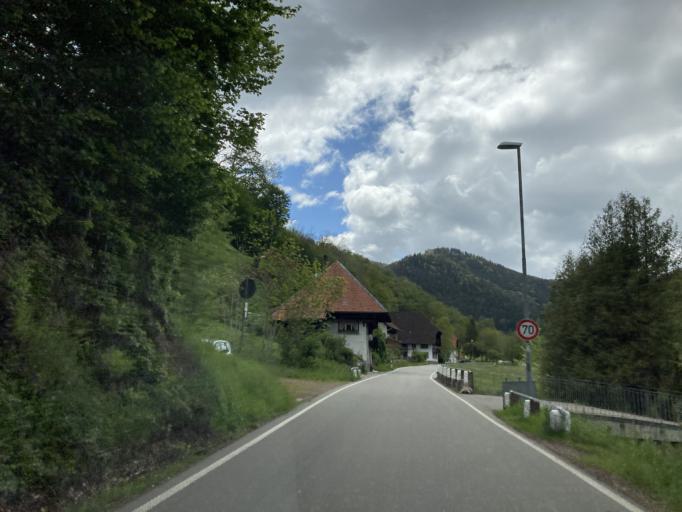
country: DE
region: Baden-Wuerttemberg
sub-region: Freiburg Region
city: Muhlenbach
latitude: 48.2098
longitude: 8.1527
